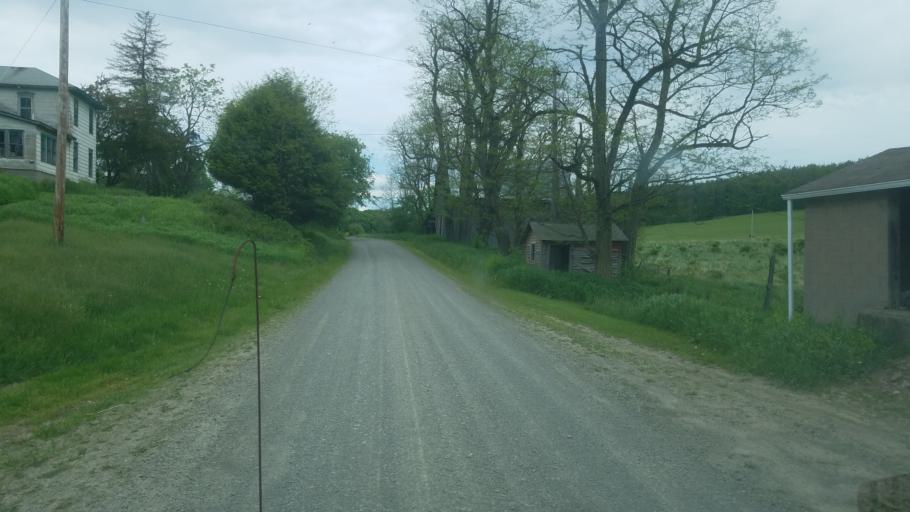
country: US
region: Pennsylvania
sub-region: Tioga County
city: Westfield
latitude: 41.8547
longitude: -77.6002
